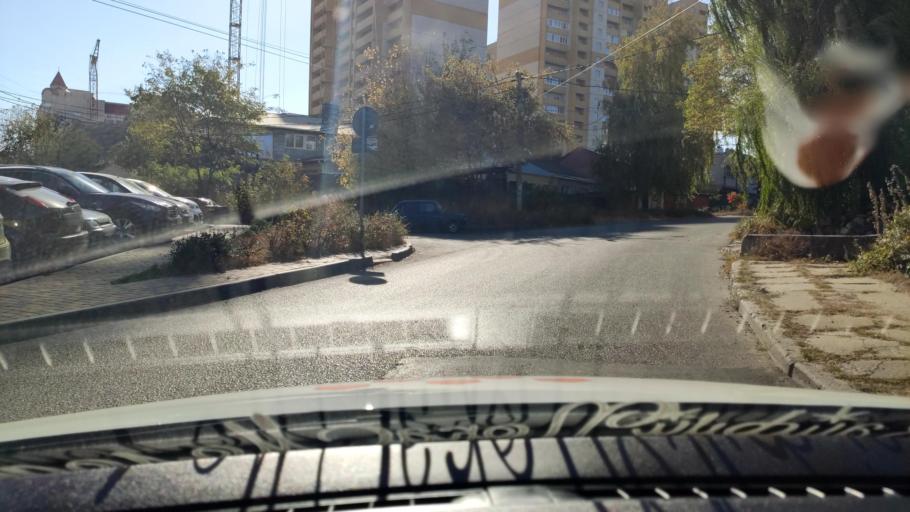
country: RU
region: Voronezj
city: Voronezh
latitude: 51.7032
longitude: 39.2049
